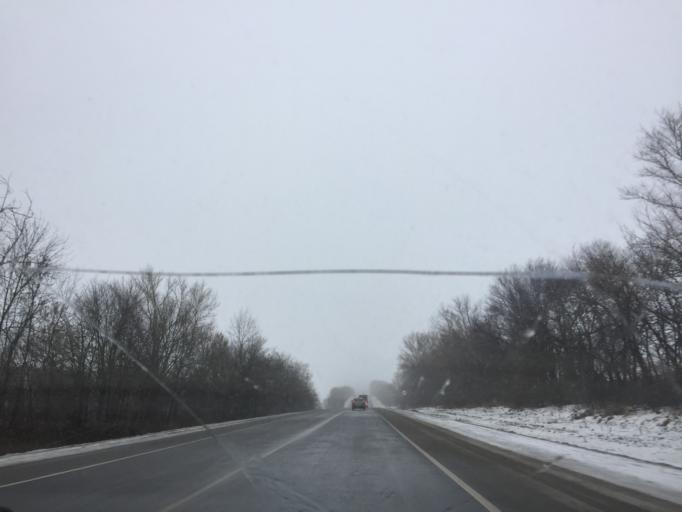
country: RU
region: Tula
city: Plavsk
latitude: 53.7972
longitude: 37.3759
